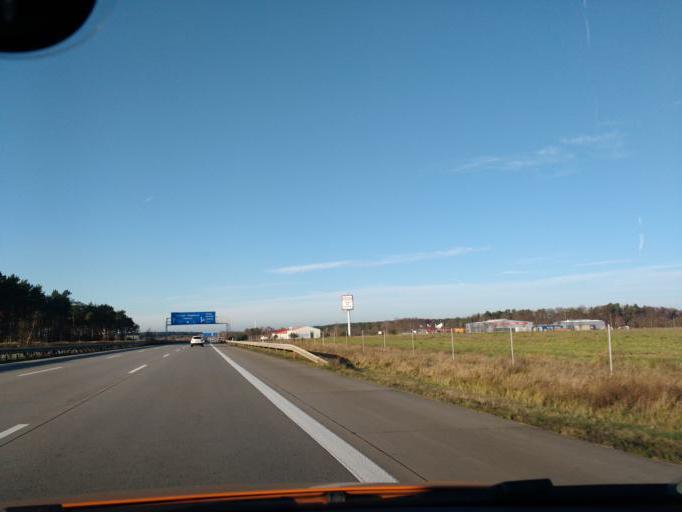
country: DE
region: Brandenburg
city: Ziesar
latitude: 52.2479
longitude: 12.2734
